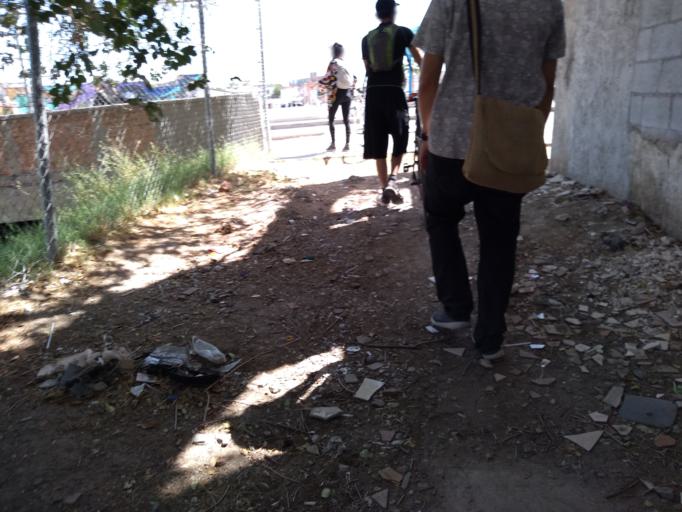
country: MX
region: Chihuahua
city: Ciudad Juarez
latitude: 31.7427
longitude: -106.4873
